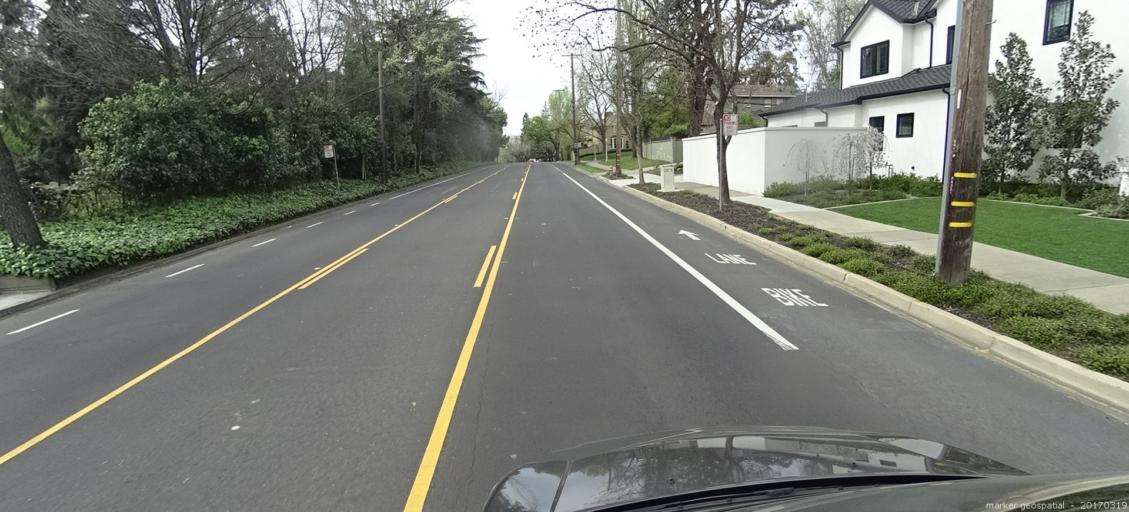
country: US
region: California
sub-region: Sacramento County
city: Sacramento
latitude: 38.5625
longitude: -121.4486
